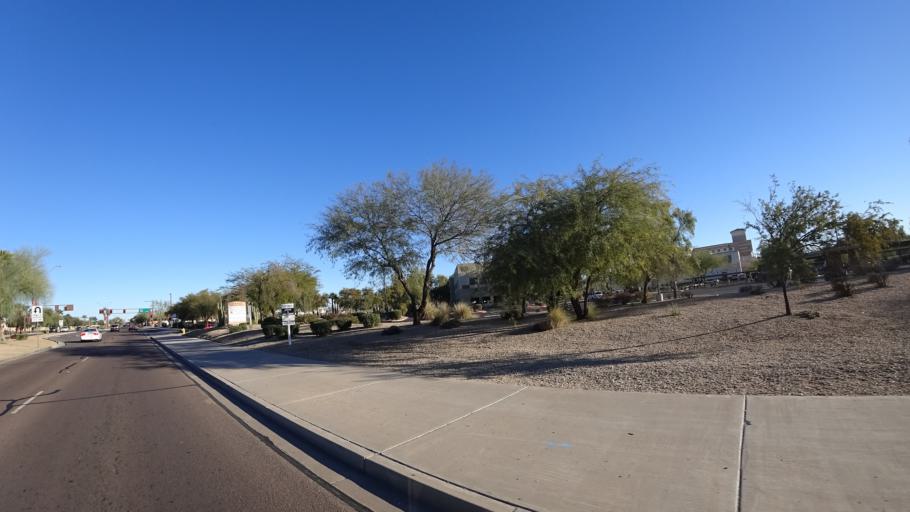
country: US
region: Arizona
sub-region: Maricopa County
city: Avondale
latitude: 33.4643
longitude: -112.3540
